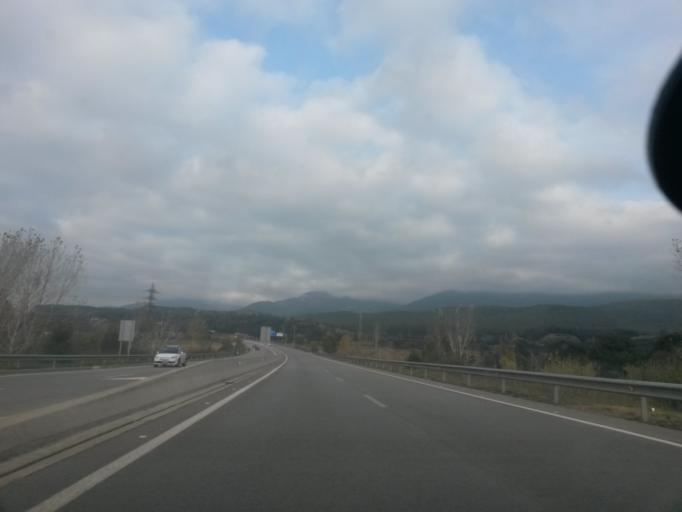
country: ES
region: Catalonia
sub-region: Provincia de Girona
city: Besalu
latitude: 42.1973
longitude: 2.7236
